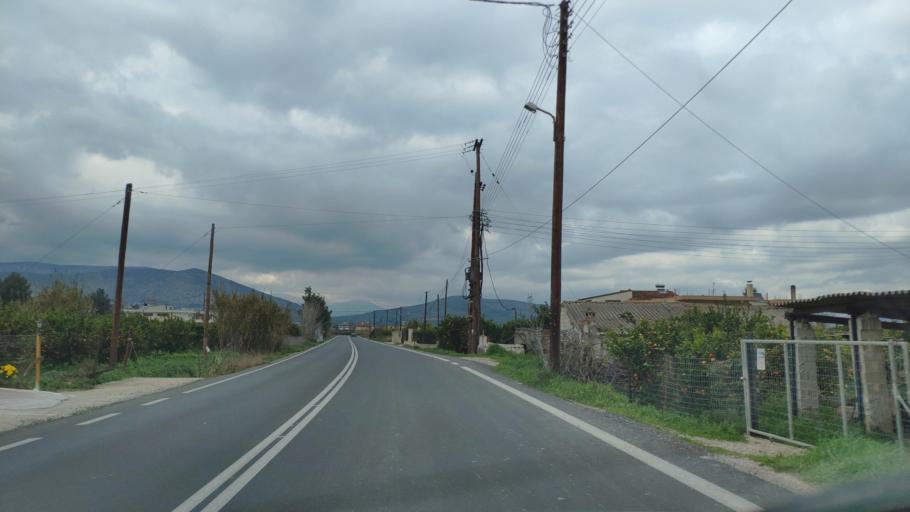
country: GR
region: Peloponnese
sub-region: Nomos Argolidos
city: Nea Kios
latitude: 37.5875
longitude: 22.7093
